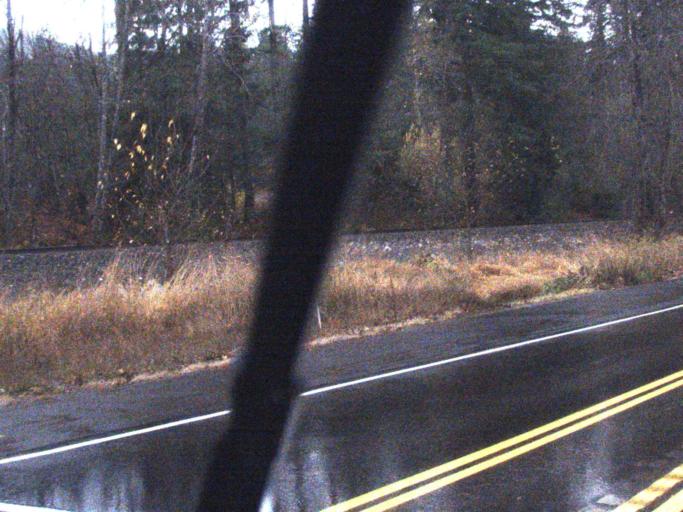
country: US
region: Washington
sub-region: Snohomish County
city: Gold Bar
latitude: 47.7135
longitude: -121.3373
